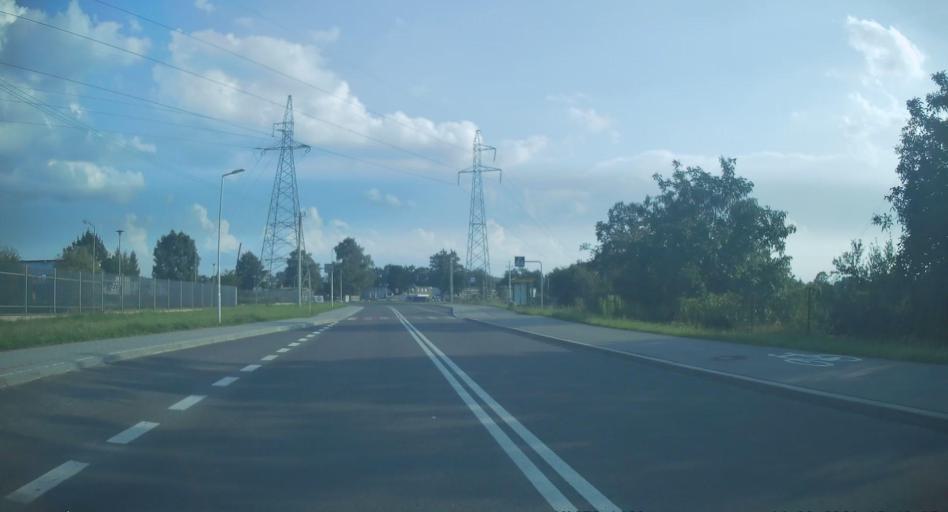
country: PL
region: Subcarpathian Voivodeship
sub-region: Powiat debicki
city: Debica
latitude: 50.0445
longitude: 21.3806
